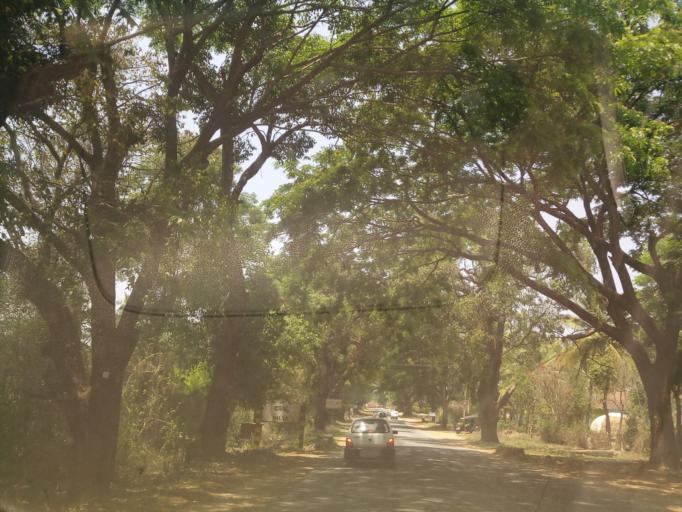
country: IN
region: Karnataka
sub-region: Hassan
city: Alur
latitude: 12.9487
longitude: 75.9448
